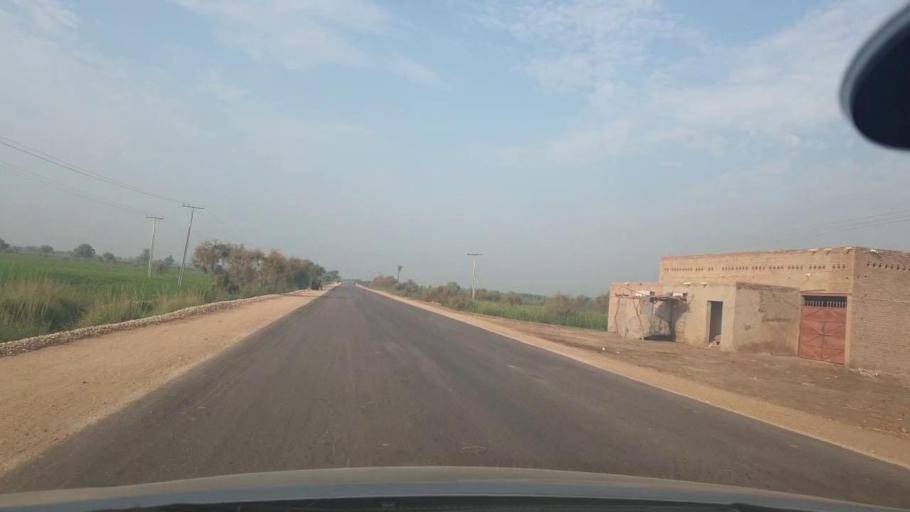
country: PK
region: Sindh
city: Jacobabad
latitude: 28.2537
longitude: 68.4075
